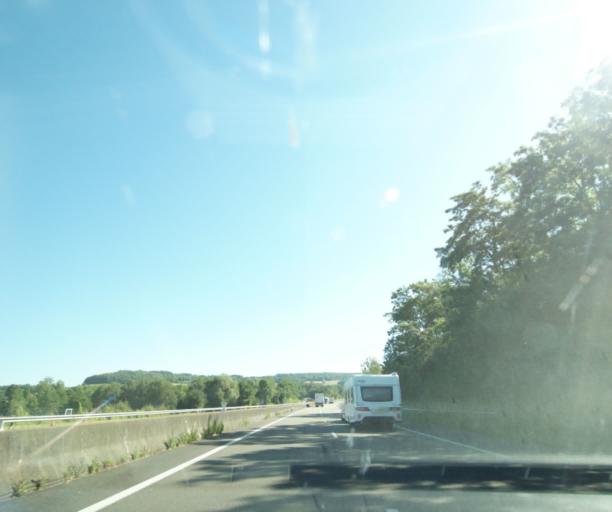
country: FR
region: Champagne-Ardenne
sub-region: Departement de la Haute-Marne
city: Rolampont
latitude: 47.9405
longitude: 5.2974
